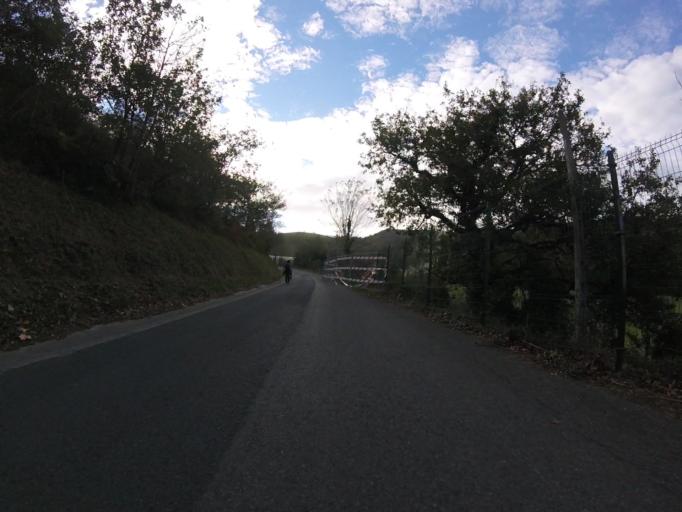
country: ES
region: Basque Country
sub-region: Provincia de Guipuzcoa
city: Errenteria
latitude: 43.3008
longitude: -1.9230
